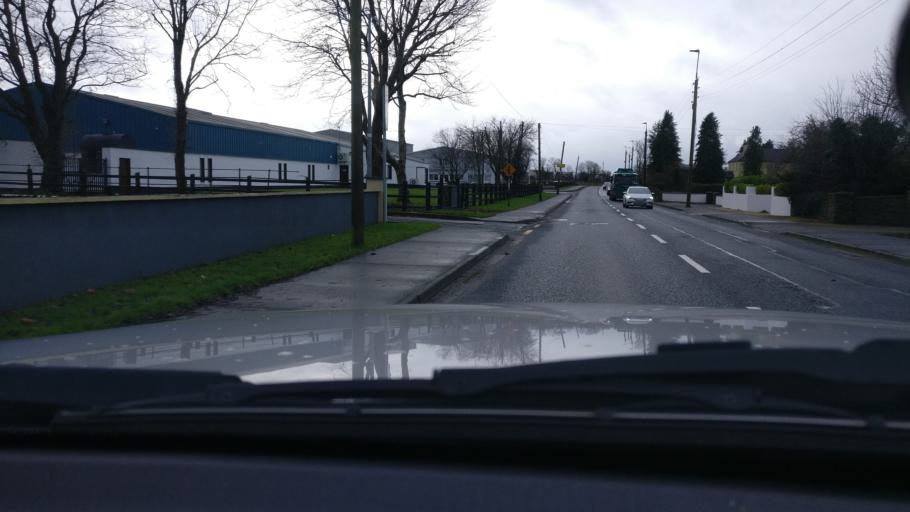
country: IE
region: Leinster
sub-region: An Longfort
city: Ballymahon
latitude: 53.5598
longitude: -7.7639
